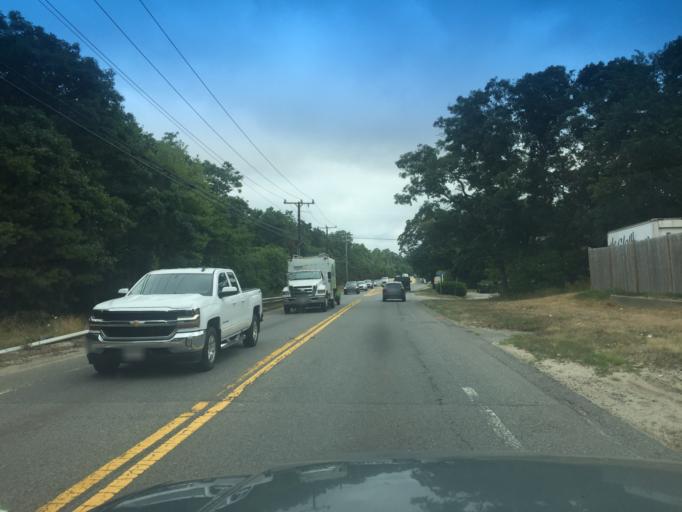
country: US
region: Massachusetts
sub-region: Barnstable County
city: Marstons Mills
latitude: 41.6460
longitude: -70.4308
